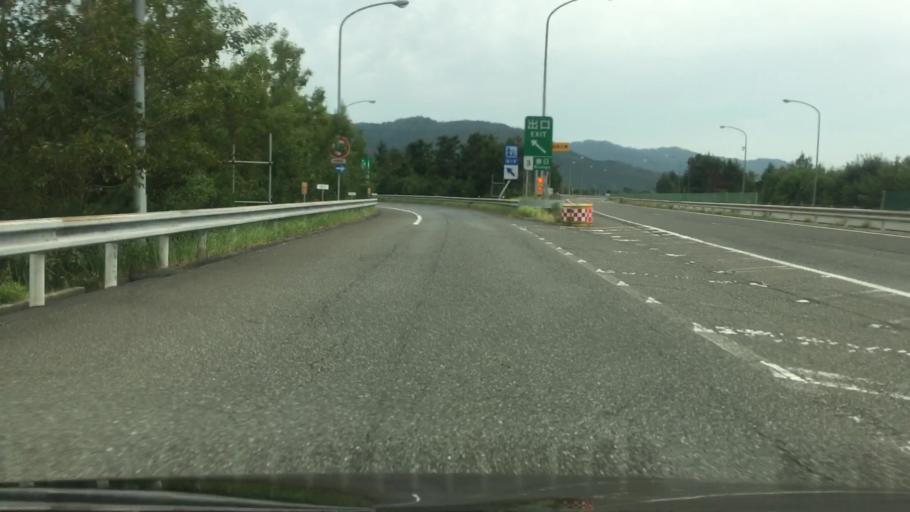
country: JP
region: Kyoto
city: Fukuchiyama
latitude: 35.1629
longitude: 135.1190
